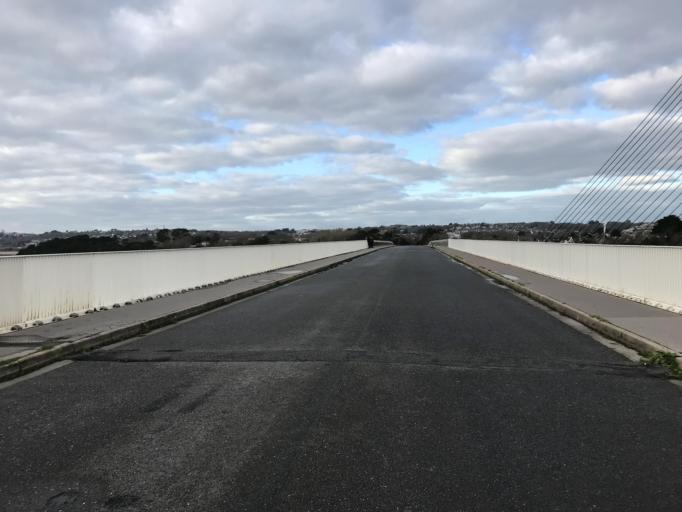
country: FR
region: Brittany
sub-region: Departement du Finistere
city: Le Relecq-Kerhuon
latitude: 48.3884
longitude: -4.4005
